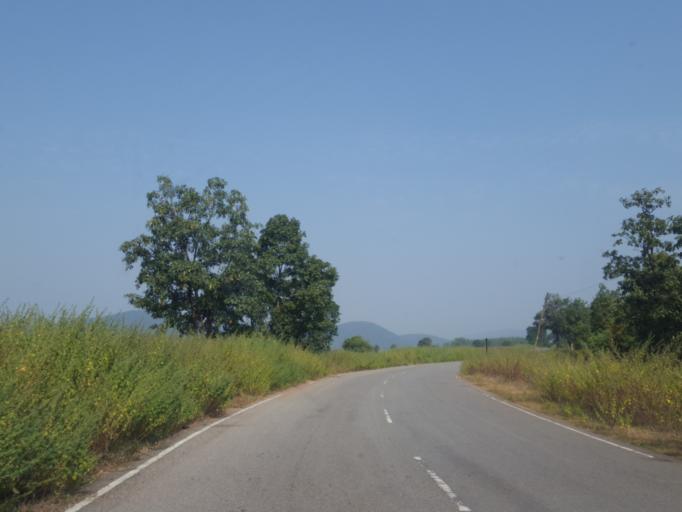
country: IN
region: Telangana
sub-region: Khammam
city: Yellandu
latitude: 17.6640
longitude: 80.2749
